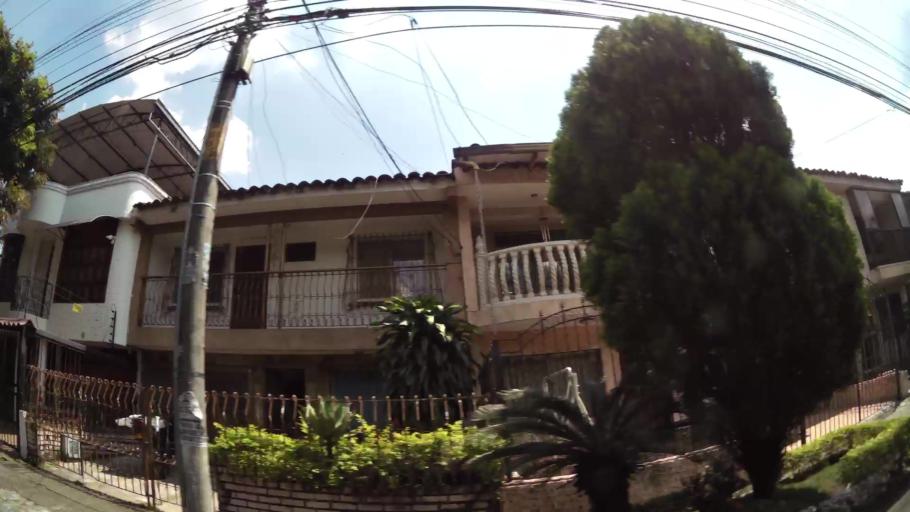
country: CO
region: Valle del Cauca
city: Cali
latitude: 3.4121
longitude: -76.5456
